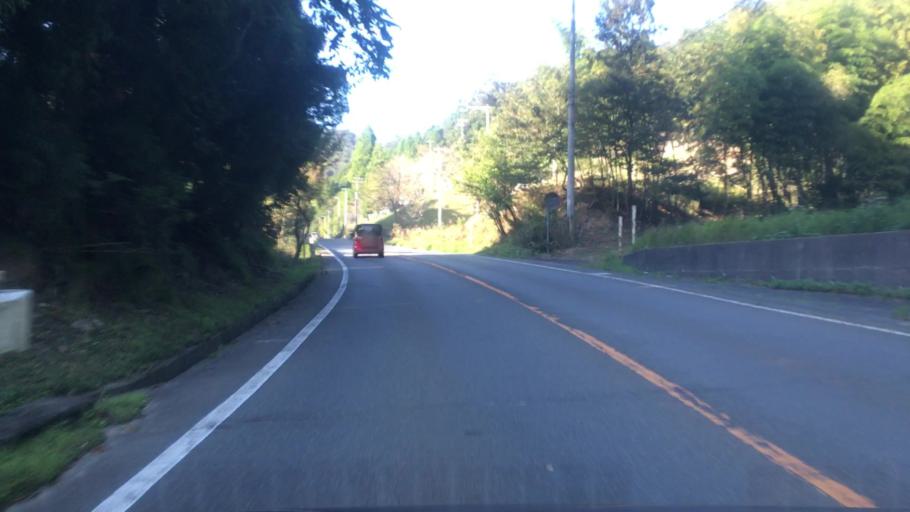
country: JP
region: Hyogo
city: Toyooka
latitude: 35.5660
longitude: 134.8528
